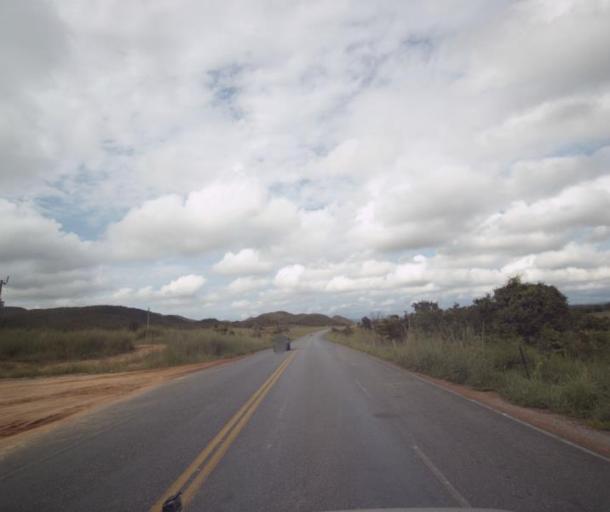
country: BR
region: Goias
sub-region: Pirenopolis
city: Pirenopolis
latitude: -15.5745
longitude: -48.6242
